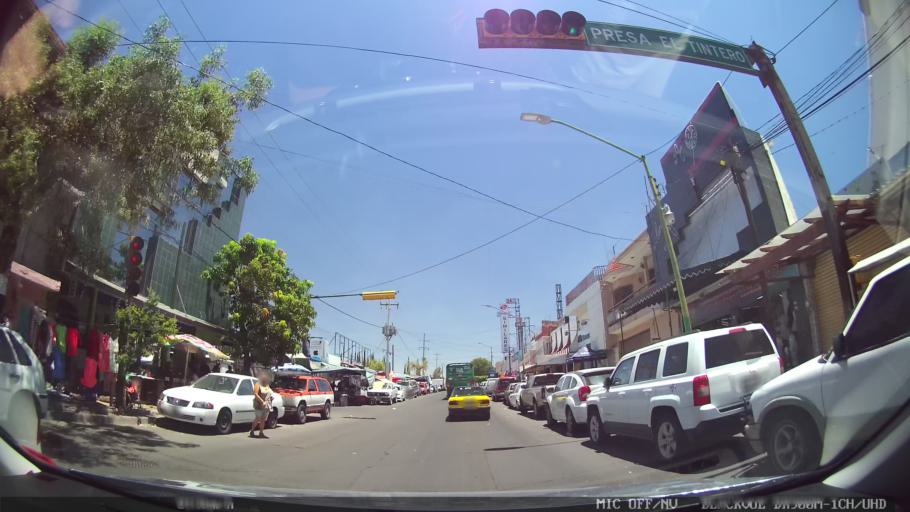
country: MX
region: Jalisco
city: Tlaquepaque
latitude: 20.6712
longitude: -103.2755
